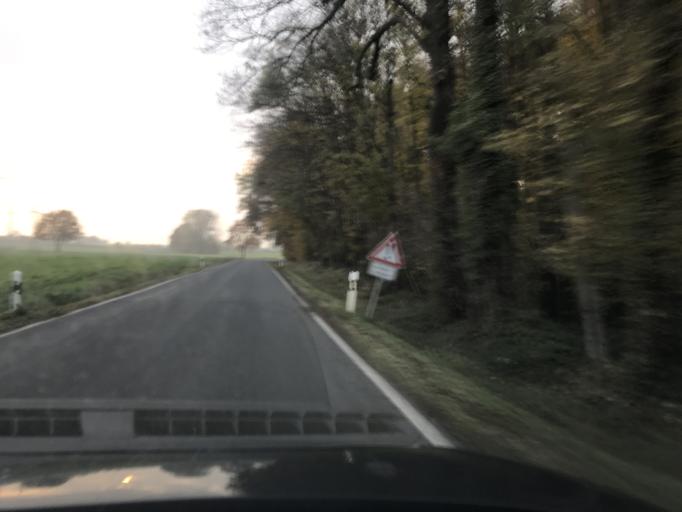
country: DE
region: North Rhine-Westphalia
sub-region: Regierungsbezirk Arnsberg
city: Welver
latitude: 51.6622
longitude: 7.9995
